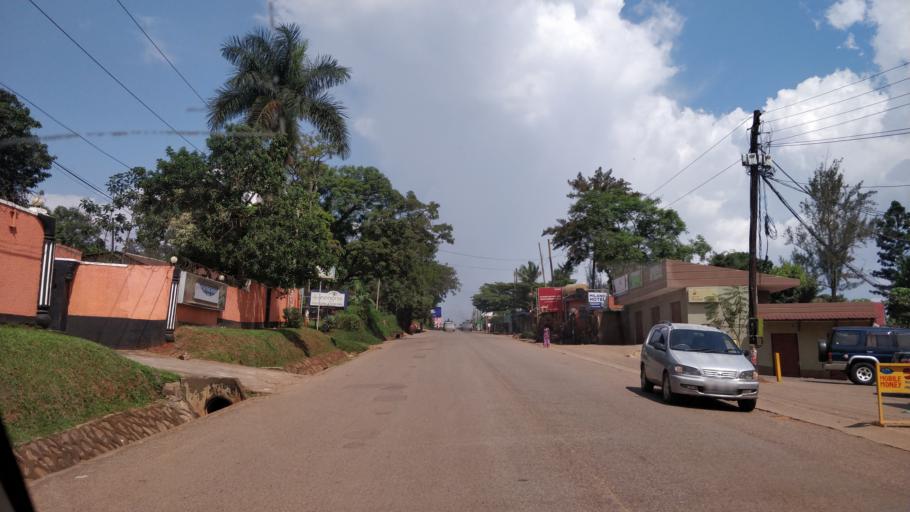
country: UG
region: Central Region
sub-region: Kampala District
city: Kampala
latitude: 0.2992
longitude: 32.6043
